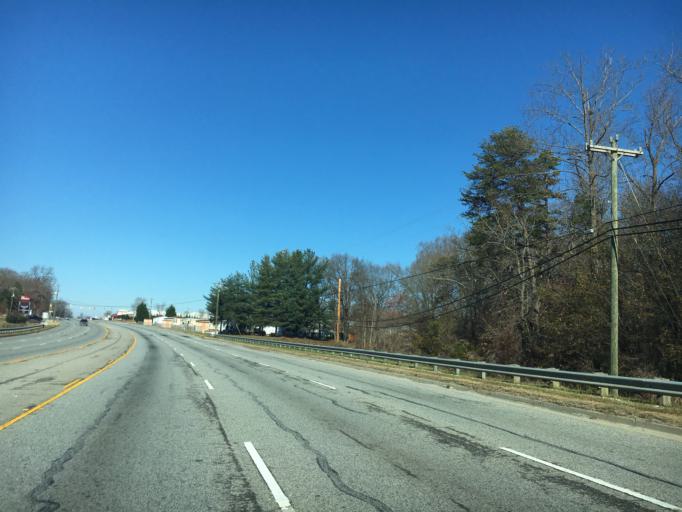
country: US
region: South Carolina
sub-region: Greenville County
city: Greer
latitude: 34.8997
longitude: -82.2360
